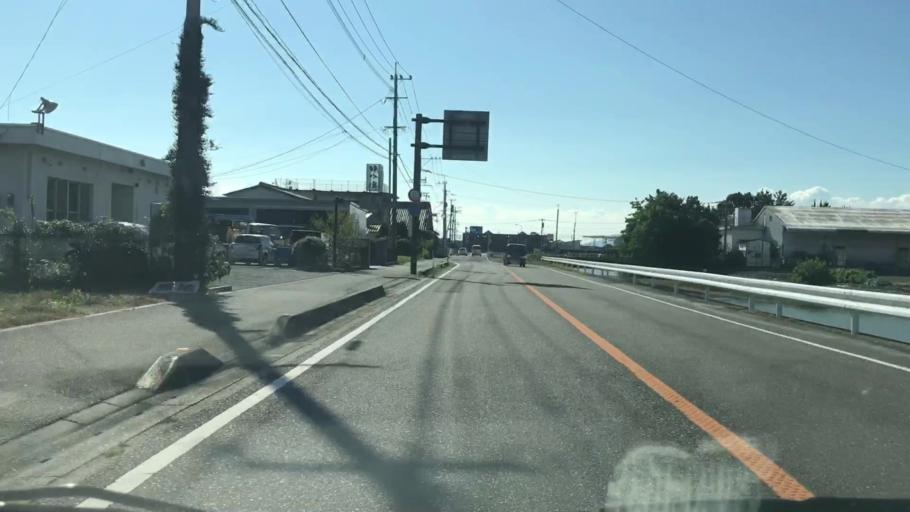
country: JP
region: Saga Prefecture
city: Okawa
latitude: 33.1916
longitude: 130.3185
